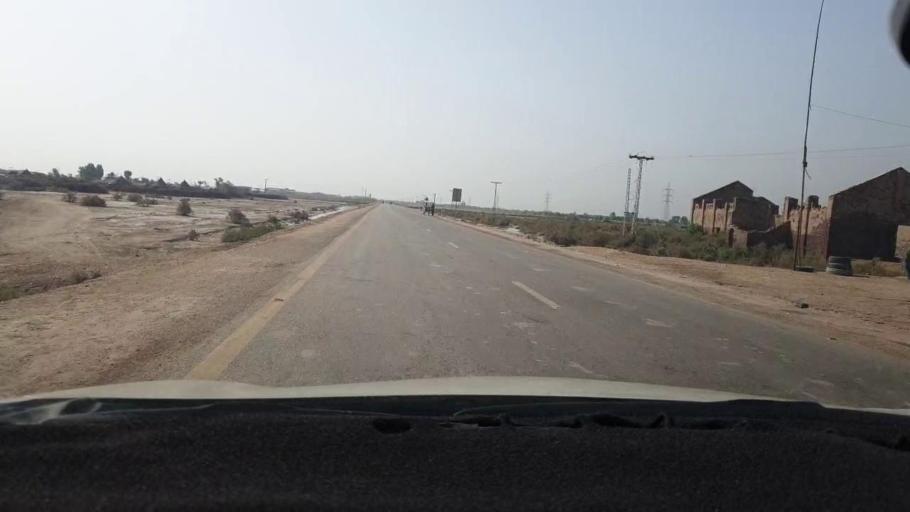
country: PK
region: Sindh
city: Sanghar
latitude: 25.9872
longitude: 68.9665
